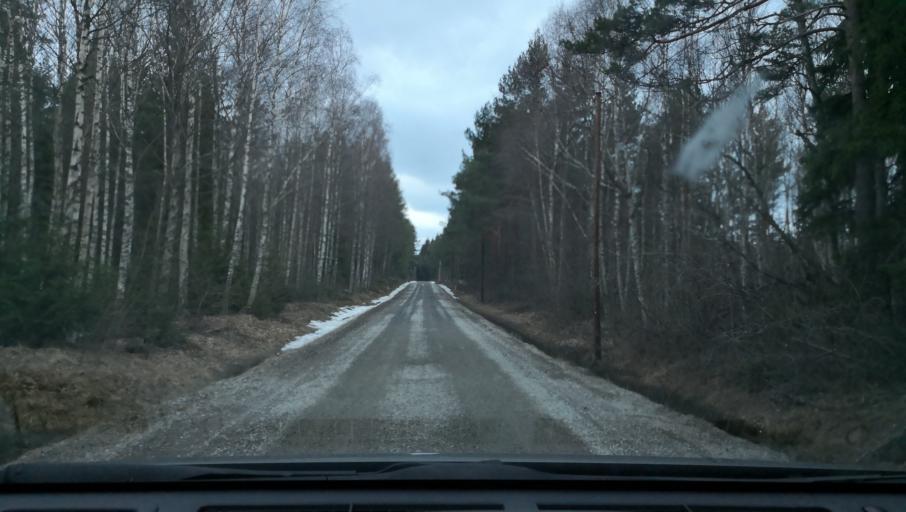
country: SE
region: Vaestmanland
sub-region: Kopings Kommun
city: Kolsva
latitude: 59.6009
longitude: 15.6666
